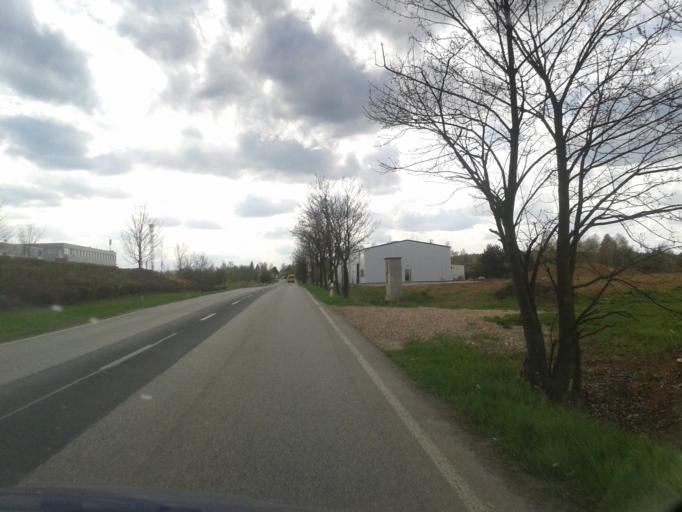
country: CZ
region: Central Bohemia
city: Rudna
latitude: 50.0213
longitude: 14.2027
